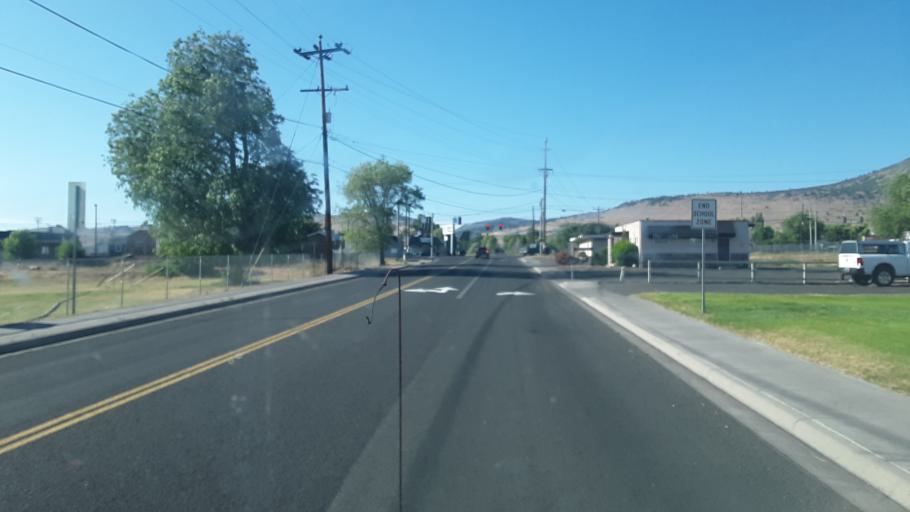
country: US
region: Oregon
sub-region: Klamath County
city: Altamont
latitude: 42.2053
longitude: -121.7378
